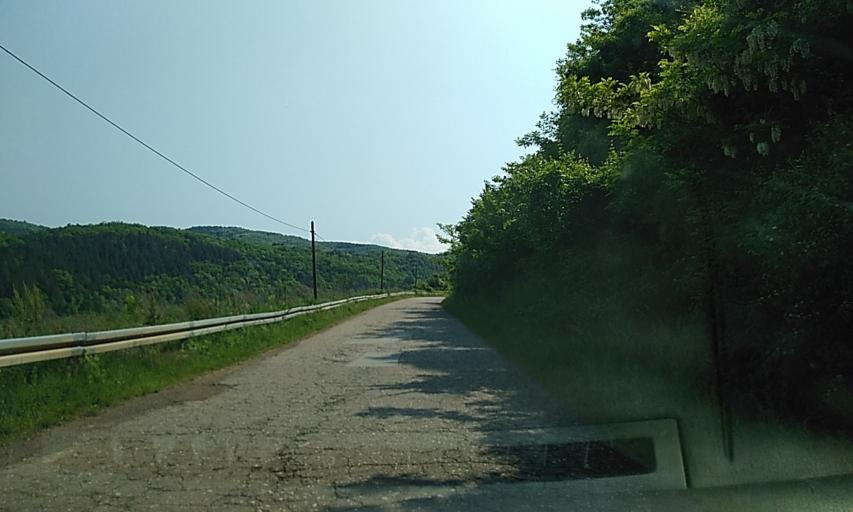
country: RS
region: Central Serbia
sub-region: Pcinjski Okrug
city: Vladicin Han
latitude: 42.7204
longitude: 22.0629
